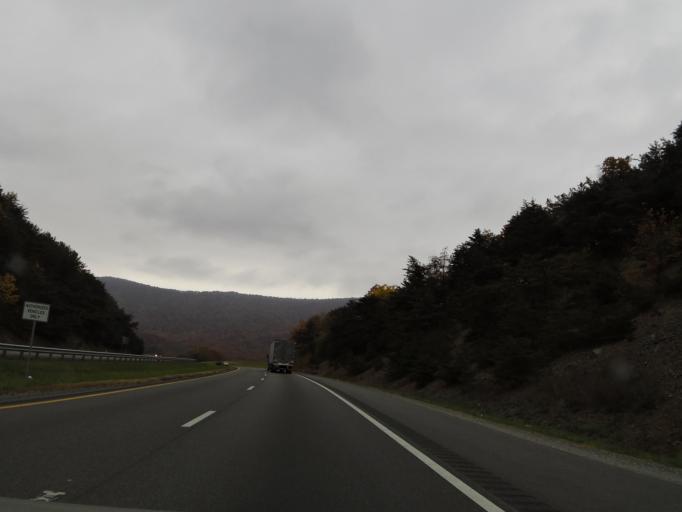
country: US
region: Virginia
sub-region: Bland County
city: Bland
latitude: 37.0264
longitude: -81.1078
